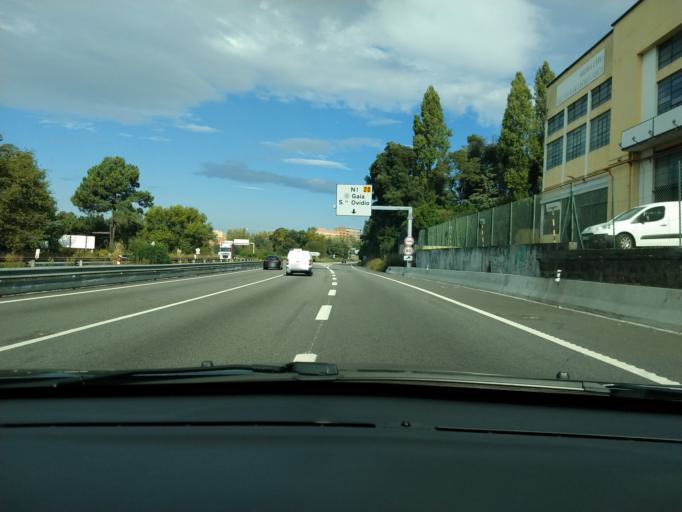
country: PT
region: Porto
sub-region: Vila Nova de Gaia
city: Vilar de Andorinho
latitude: 41.1077
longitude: -8.6045
